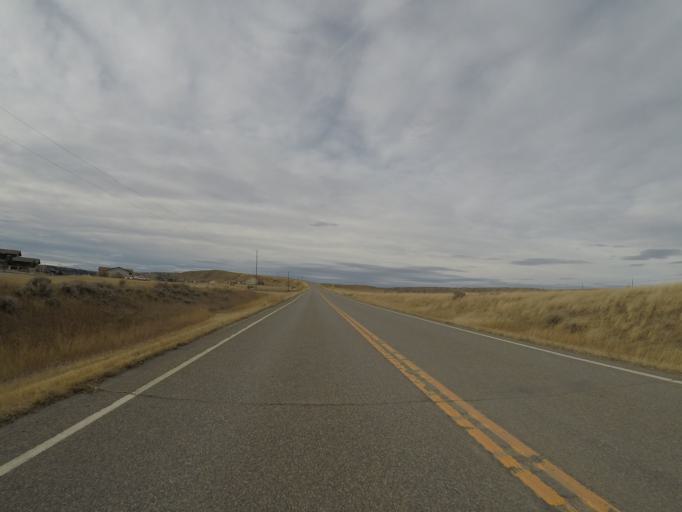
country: US
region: Montana
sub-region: Yellowstone County
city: Laurel
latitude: 45.8425
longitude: -108.7240
